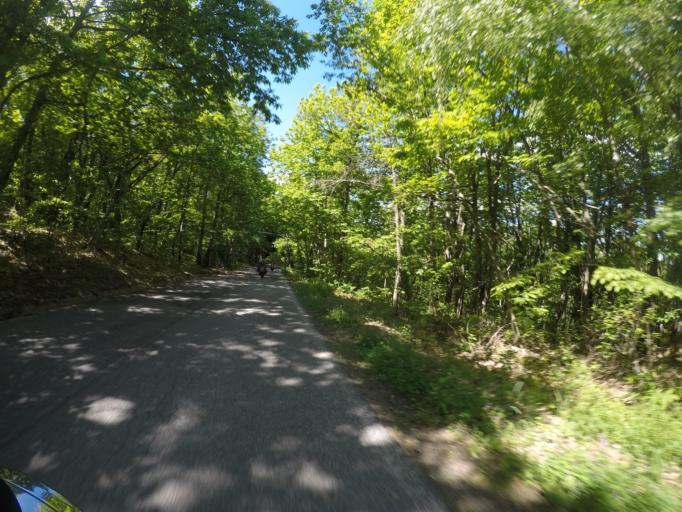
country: IT
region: Tuscany
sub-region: Provincia di Lucca
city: Careggine
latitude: 44.1135
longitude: 10.3311
